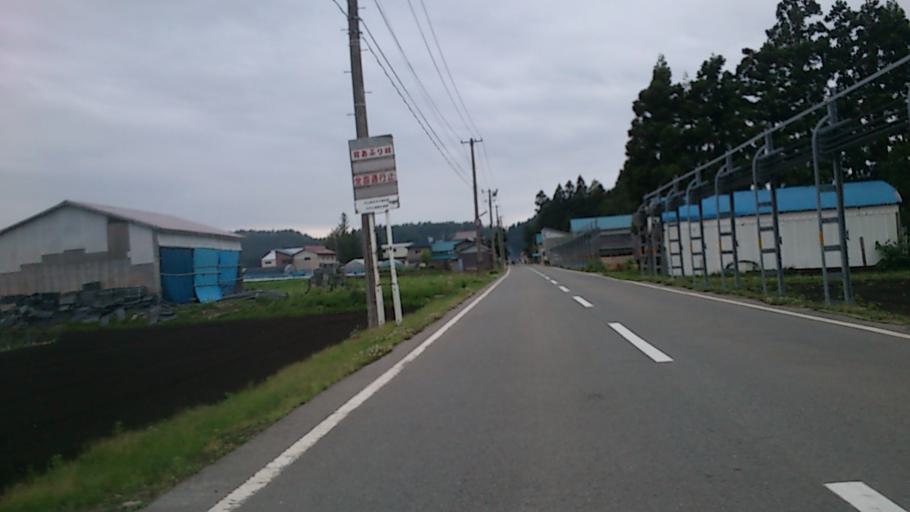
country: JP
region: Yamagata
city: Obanazawa
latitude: 38.5761
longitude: 140.4859
